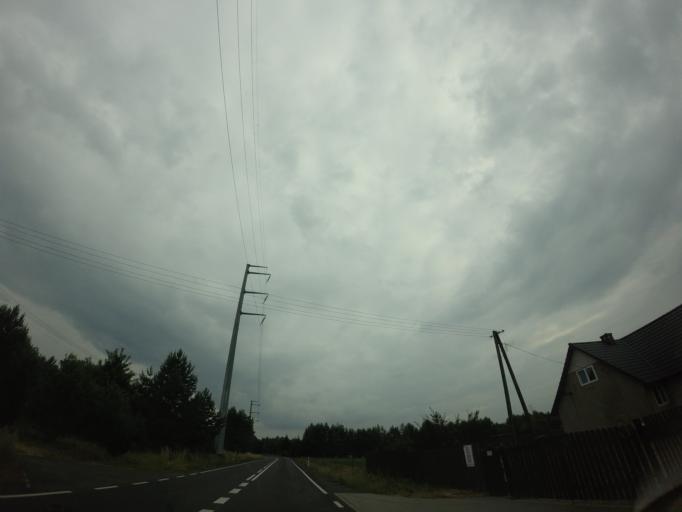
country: PL
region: West Pomeranian Voivodeship
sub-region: Powiat drawski
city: Czaplinek
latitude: 53.5141
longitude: 16.2232
